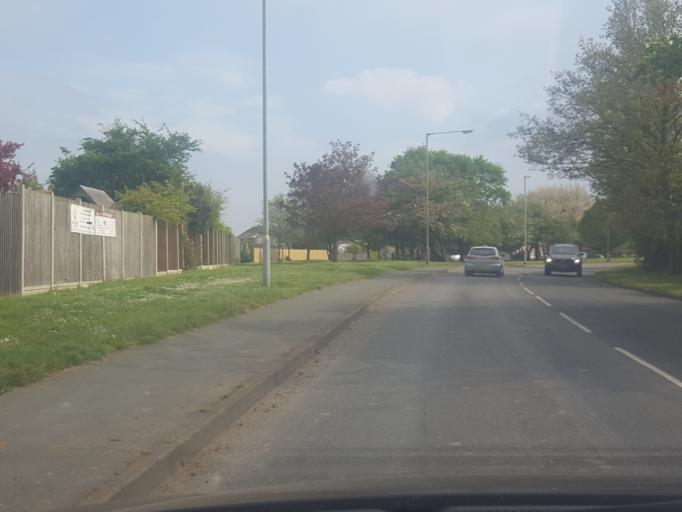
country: GB
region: England
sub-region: Essex
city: Frinton-on-Sea
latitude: 51.8485
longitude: 1.2481
